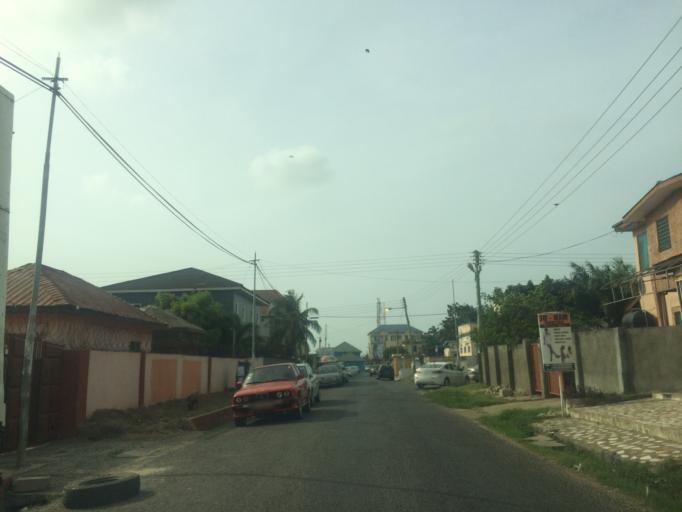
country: GH
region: Greater Accra
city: Accra
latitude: 5.5559
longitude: -0.1799
